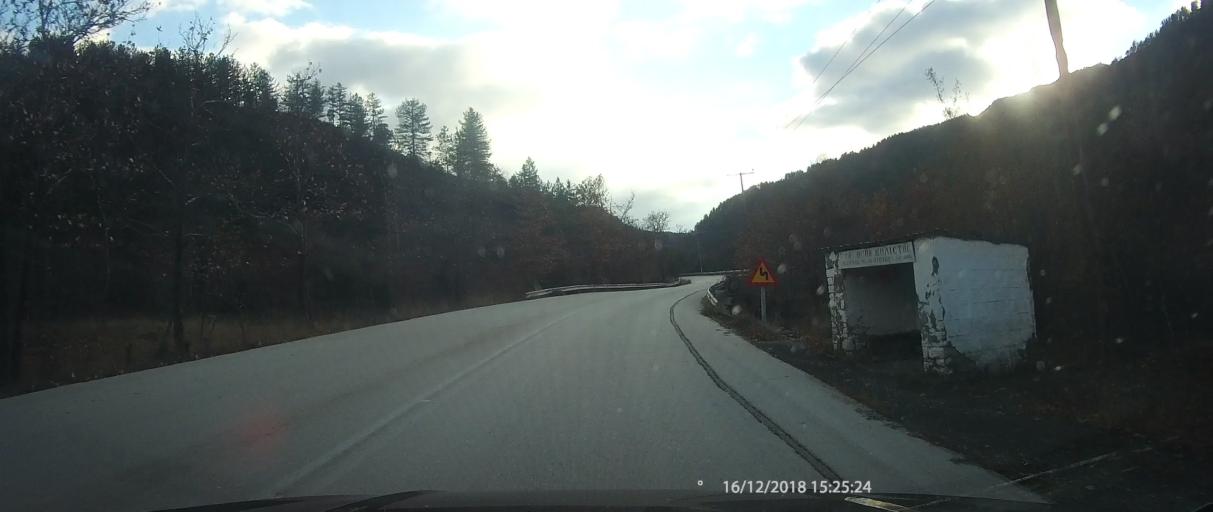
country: GR
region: Epirus
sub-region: Nomos Ioanninon
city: Konitsa
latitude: 40.1286
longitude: 20.7826
